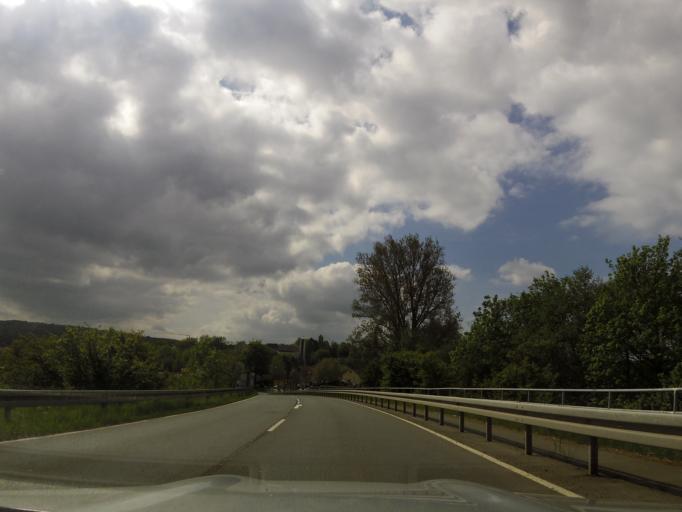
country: DE
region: Hesse
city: Burgsolms
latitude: 50.5448
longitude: 8.4085
